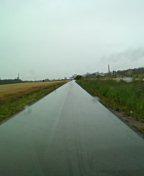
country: SE
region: Vaestmanland
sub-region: Kopings Kommun
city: Koping
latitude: 59.4898
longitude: 16.0429
